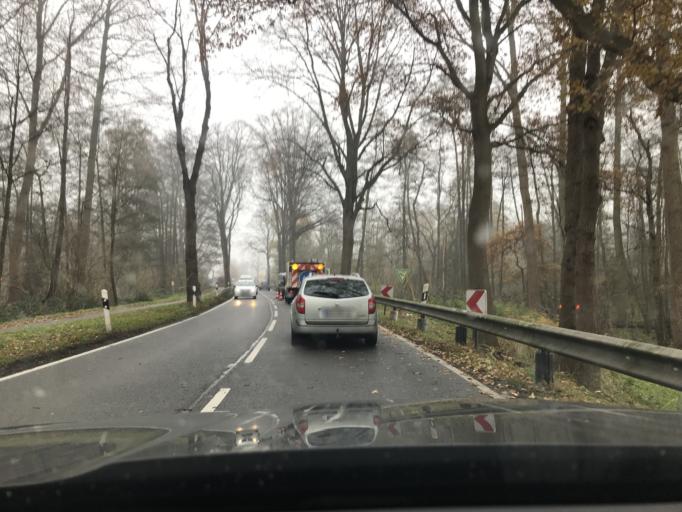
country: DE
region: North Rhine-Westphalia
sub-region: Regierungsbezirk Dusseldorf
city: Nettetal
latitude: 51.2819
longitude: 6.2683
